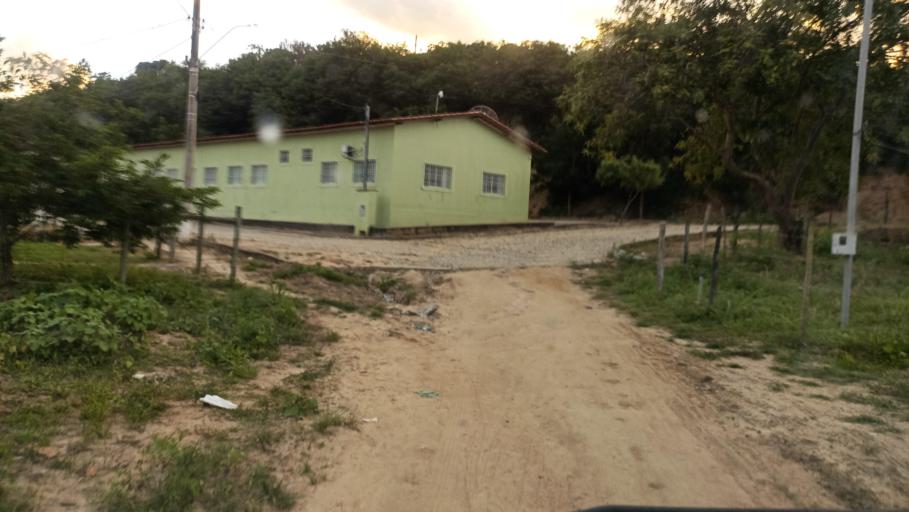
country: BR
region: Minas Gerais
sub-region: Almenara
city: Almenara
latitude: -16.5205
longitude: -40.4416
